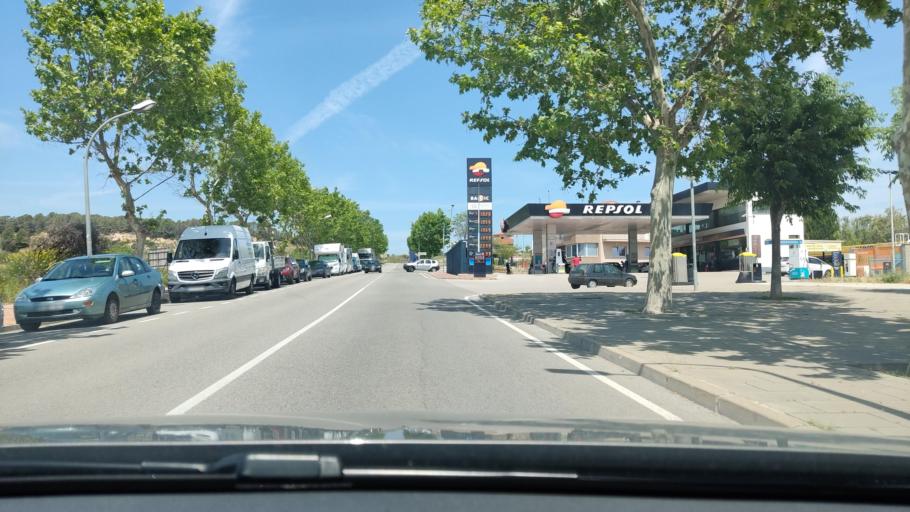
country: ES
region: Catalonia
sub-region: Provincia de Barcelona
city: Sant Sadurni d'Anoia
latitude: 41.4282
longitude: 1.7793
